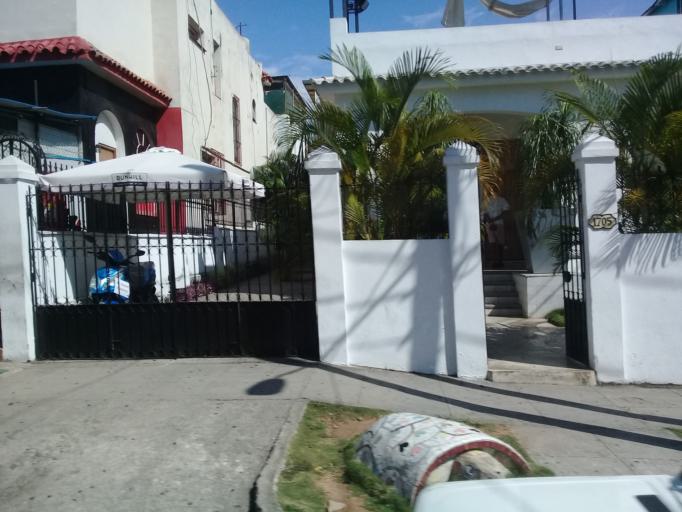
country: CU
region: La Habana
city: Havana
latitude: 23.1201
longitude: -82.4069
